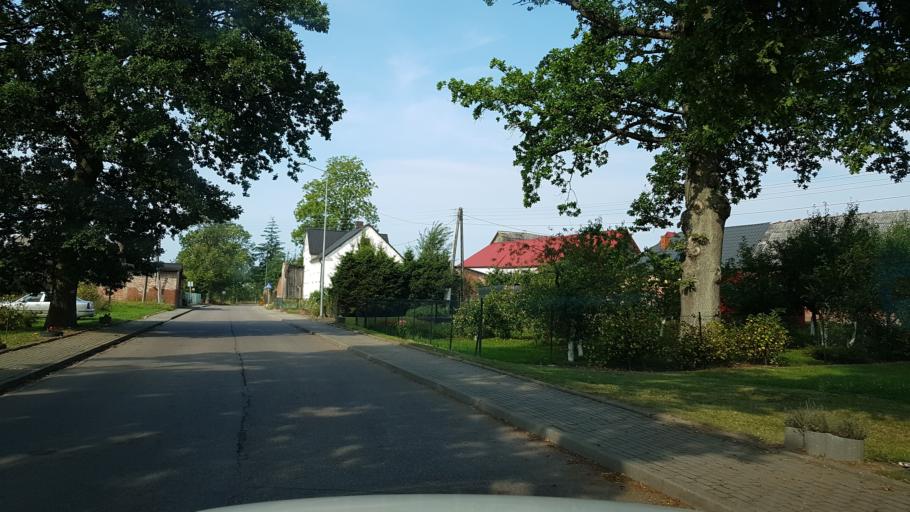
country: PL
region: West Pomeranian Voivodeship
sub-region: Powiat slawienski
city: Slawno
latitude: 54.5094
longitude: 16.6218
